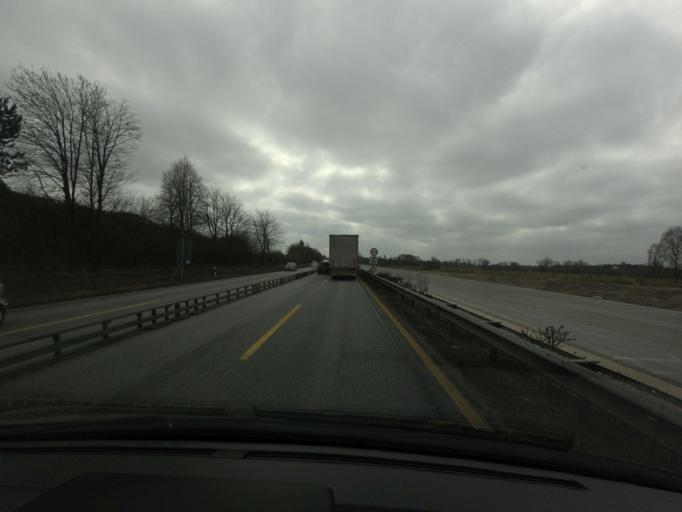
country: DE
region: Schleswig-Holstein
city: Alveslohe
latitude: 53.8147
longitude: 9.9244
